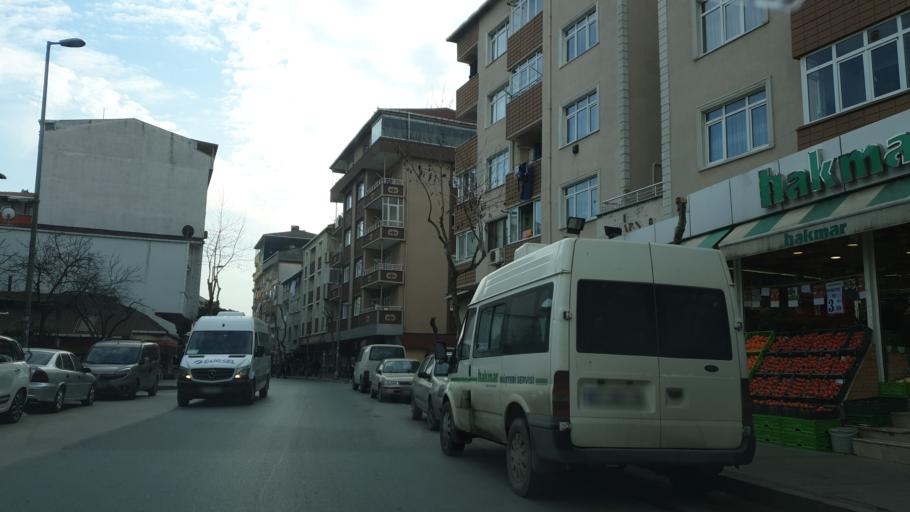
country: TR
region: Istanbul
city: Pendik
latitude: 40.8779
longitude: 29.2738
